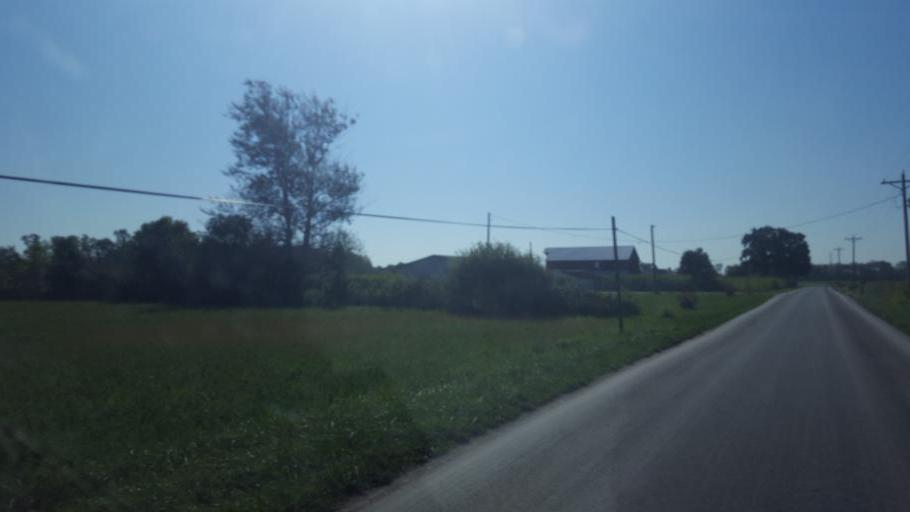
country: US
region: Ohio
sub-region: Hardin County
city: Kenton
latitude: 40.5698
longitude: -83.4516
